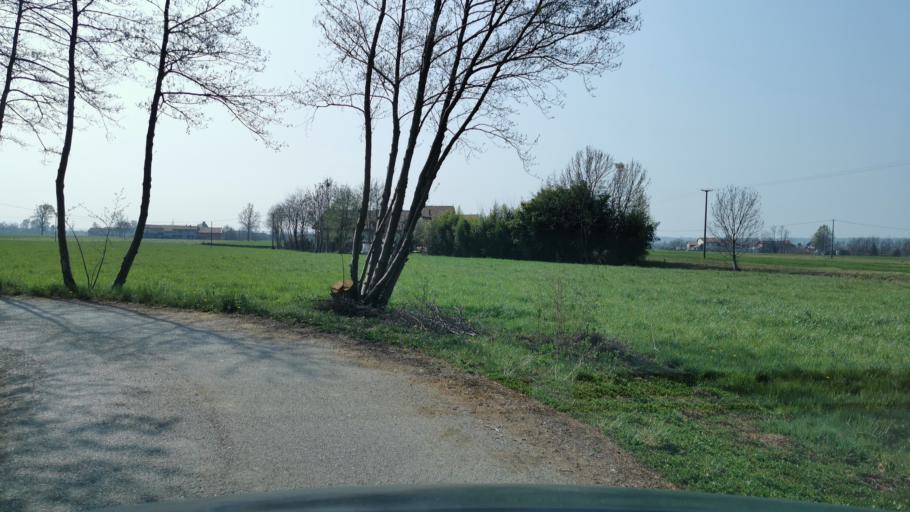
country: IT
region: Piedmont
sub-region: Provincia di Torino
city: Favria
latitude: 45.3189
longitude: 7.6978
